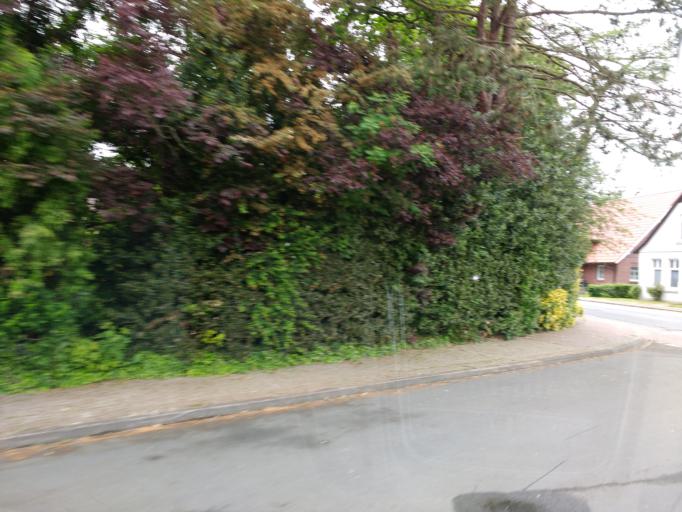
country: DE
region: Lower Saxony
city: Sillenstede
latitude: 53.6093
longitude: 7.9546
